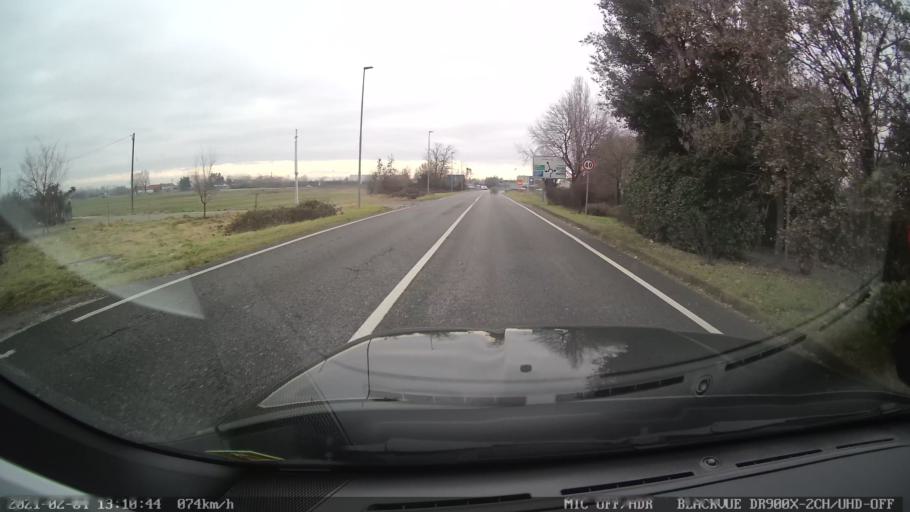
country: IT
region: Piedmont
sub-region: Provincia di Novara
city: Novara
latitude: 45.4661
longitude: 8.6097
